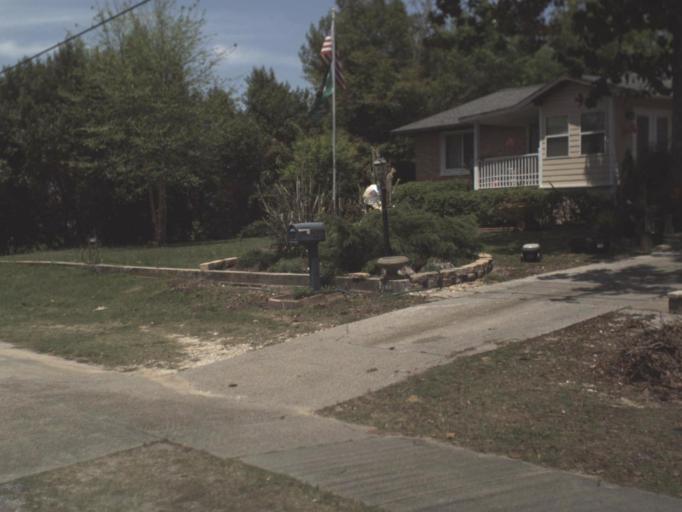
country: US
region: Florida
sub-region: Escambia County
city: East Pensacola Heights
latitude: 30.4498
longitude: -87.1900
